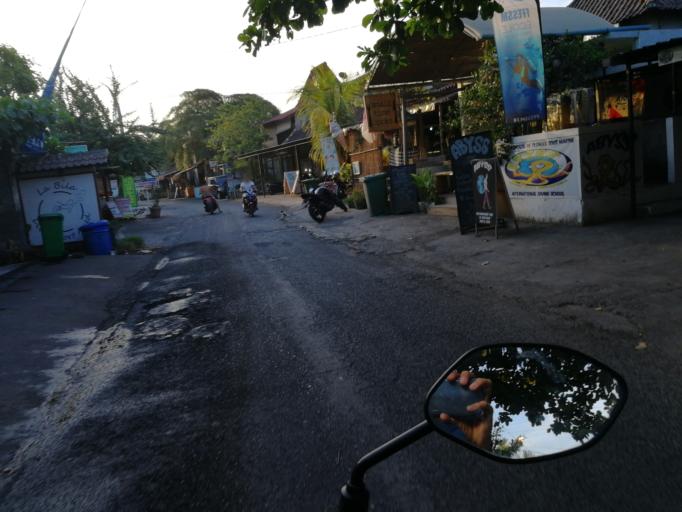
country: ID
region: Bali
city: Biaslantang Kaler
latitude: -8.3358
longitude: 115.6494
